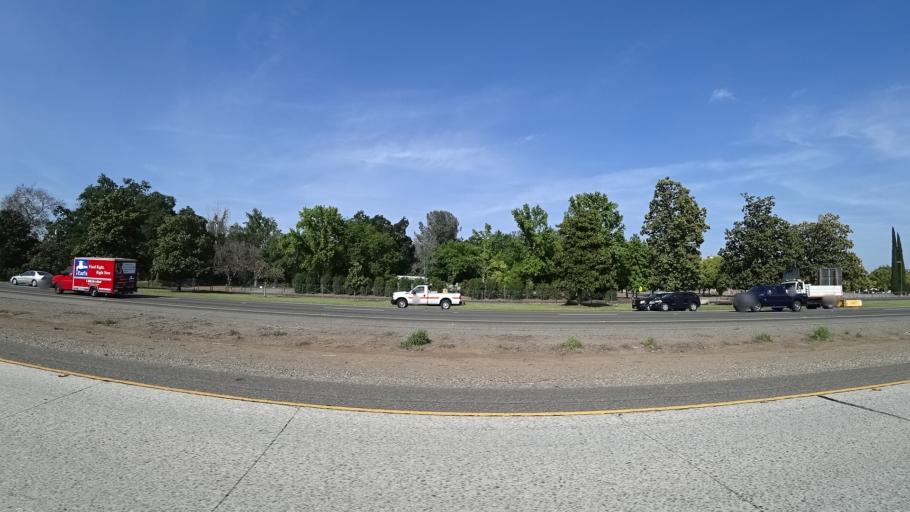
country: US
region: California
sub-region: Butte County
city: Chico
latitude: 39.7074
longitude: -121.7931
